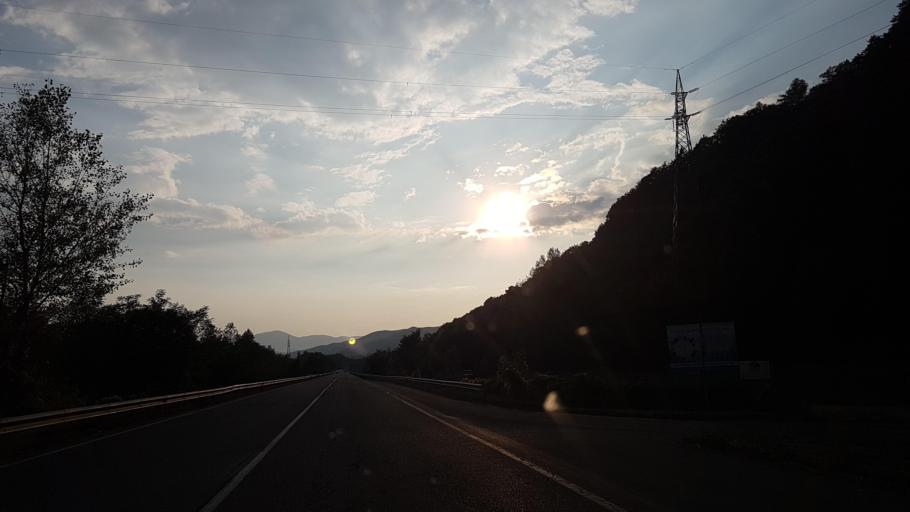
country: IT
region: Emilia-Romagna
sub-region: Provincia di Parma
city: Borgo Val di Taro
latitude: 44.4968
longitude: 9.7959
